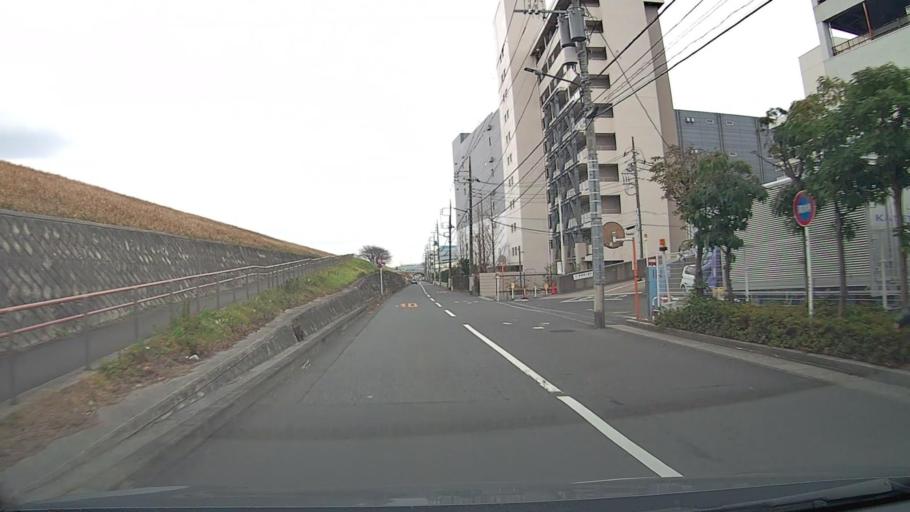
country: JP
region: Saitama
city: Shimotoda
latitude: 35.7968
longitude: 139.6709
